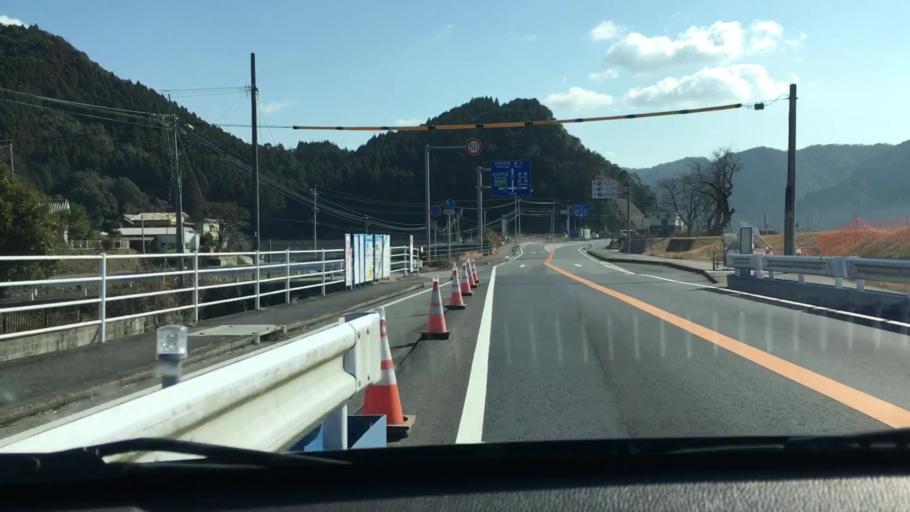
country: JP
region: Oita
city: Saiki
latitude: 32.9589
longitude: 131.8434
